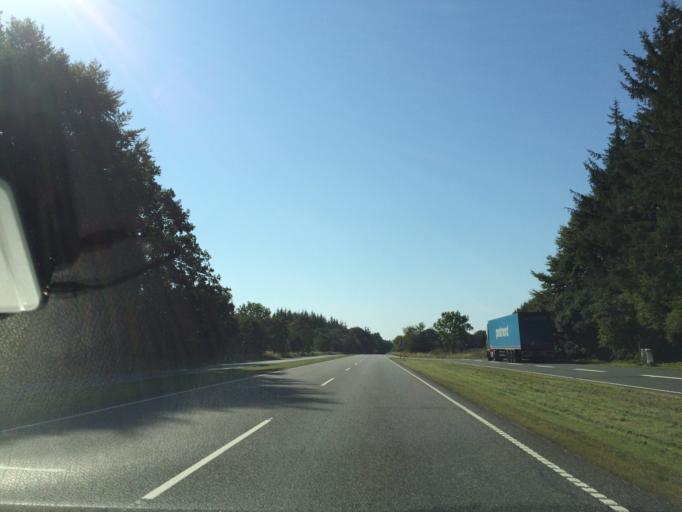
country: DK
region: South Denmark
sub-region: Kolding Kommune
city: Kolding
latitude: 55.5210
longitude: 9.4992
